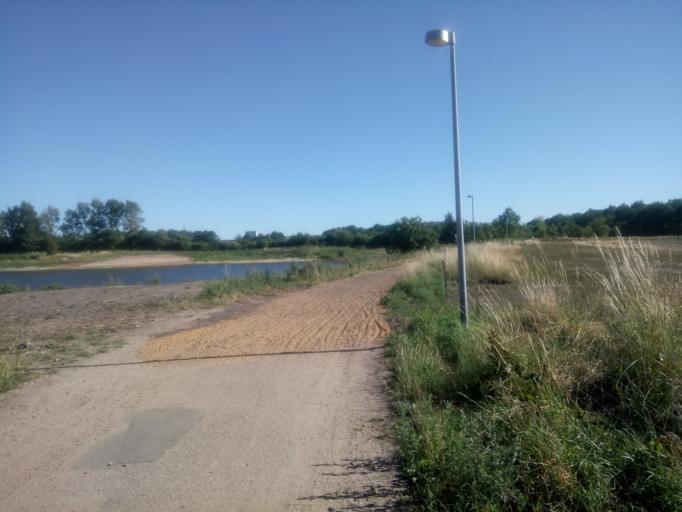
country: DK
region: Central Jutland
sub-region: Herning Kommune
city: Herning
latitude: 56.1516
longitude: 8.9775
